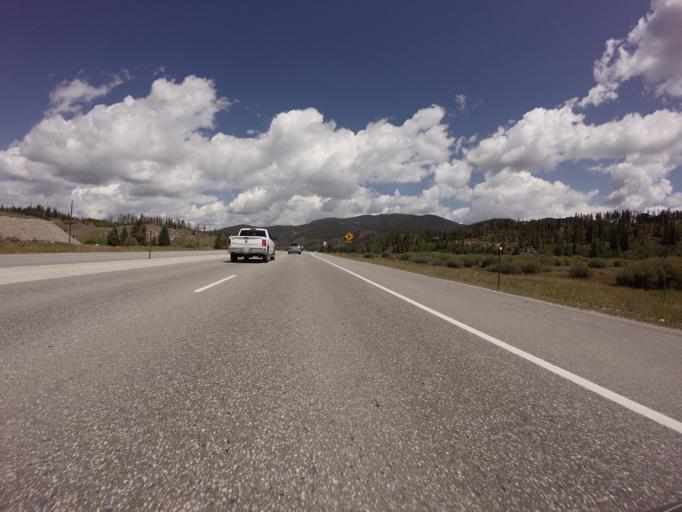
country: US
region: Colorado
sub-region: Summit County
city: Breckenridge
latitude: 39.5362
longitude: -106.0425
